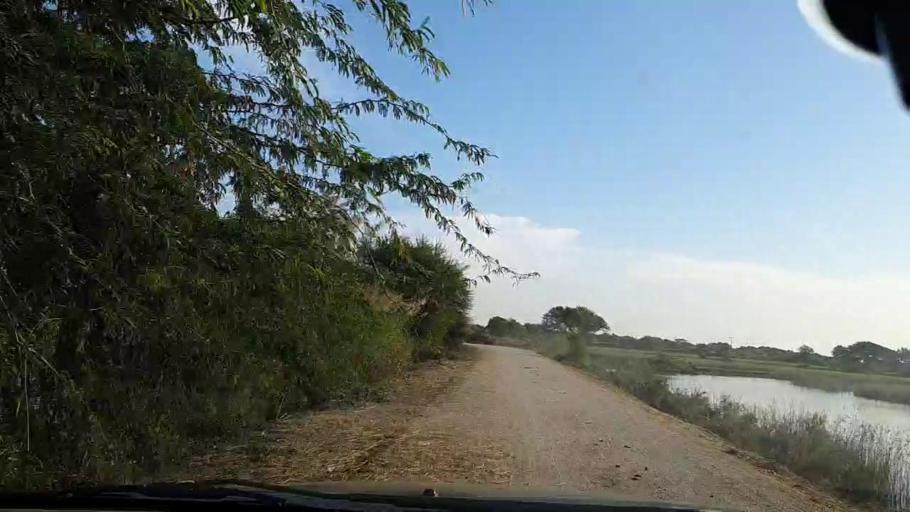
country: PK
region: Sindh
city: Mirpur Batoro
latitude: 24.6527
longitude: 68.2936
